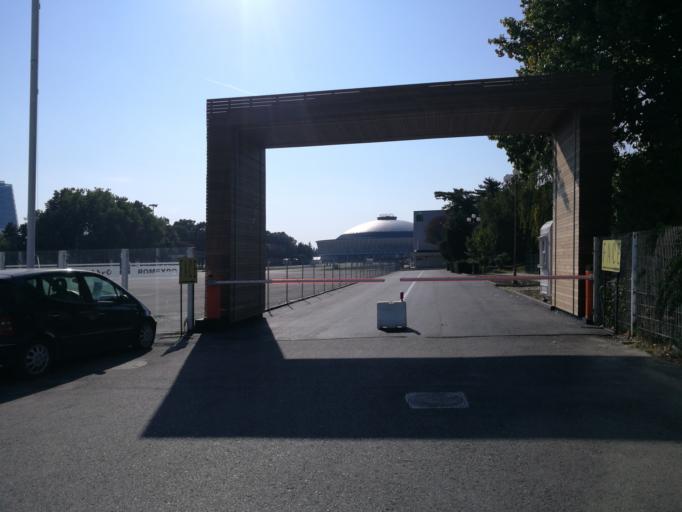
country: RO
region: Bucuresti
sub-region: Municipiul Bucuresti
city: Bucuresti
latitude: 44.4779
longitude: 26.0707
